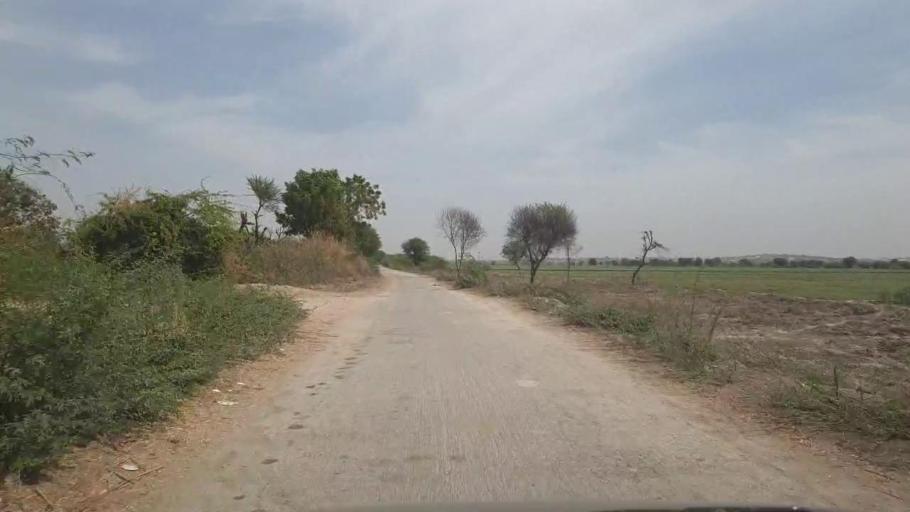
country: PK
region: Sindh
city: Kunri
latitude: 25.2237
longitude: 69.6955
